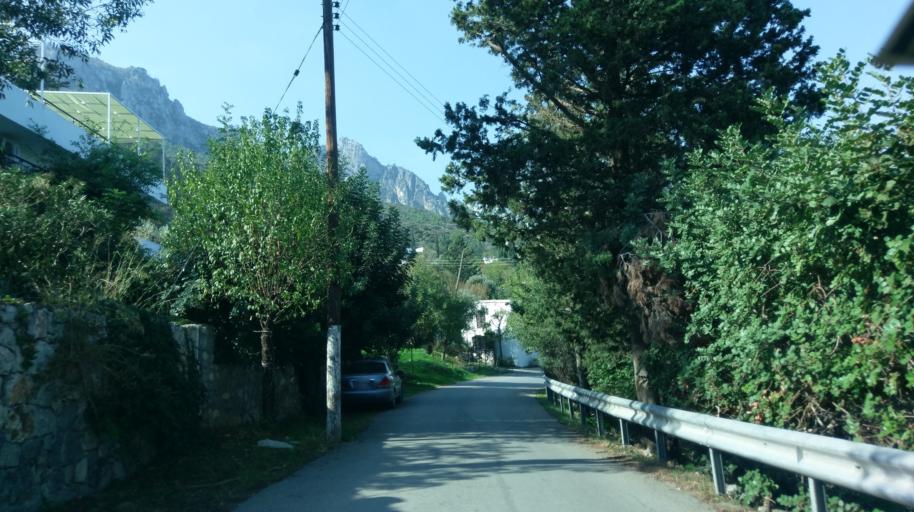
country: CY
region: Keryneia
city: Kyrenia
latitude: 35.3177
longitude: 33.2593
